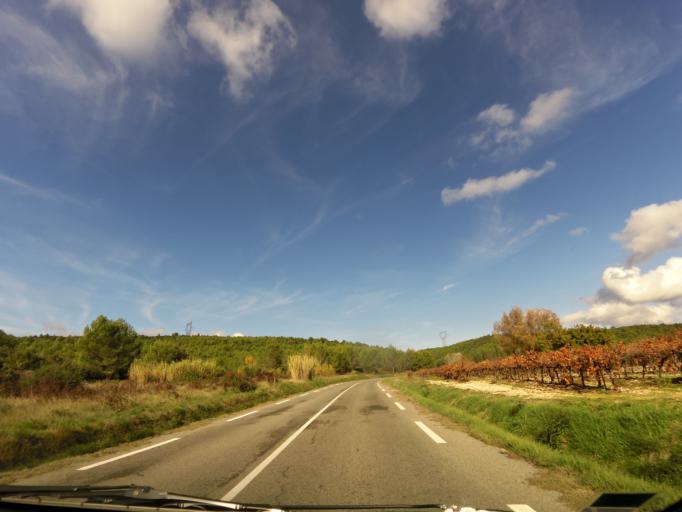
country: FR
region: Languedoc-Roussillon
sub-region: Departement du Gard
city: Villevieille
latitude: 43.8414
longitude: 4.0985
